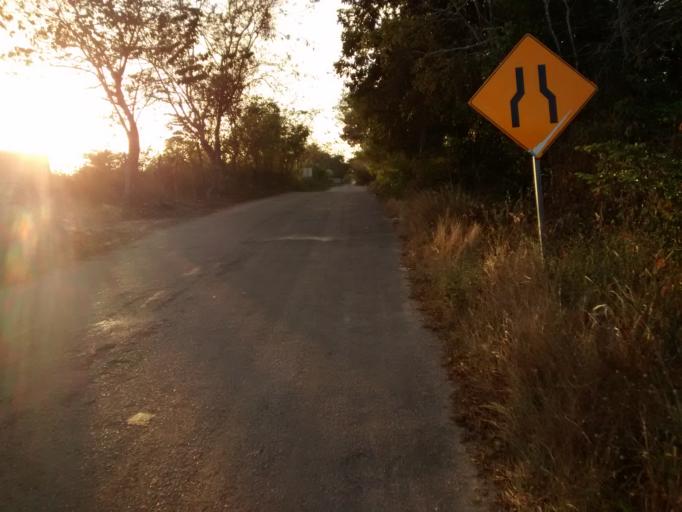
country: MX
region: Yucatan
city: Valladolid
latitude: 20.6821
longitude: -88.1674
